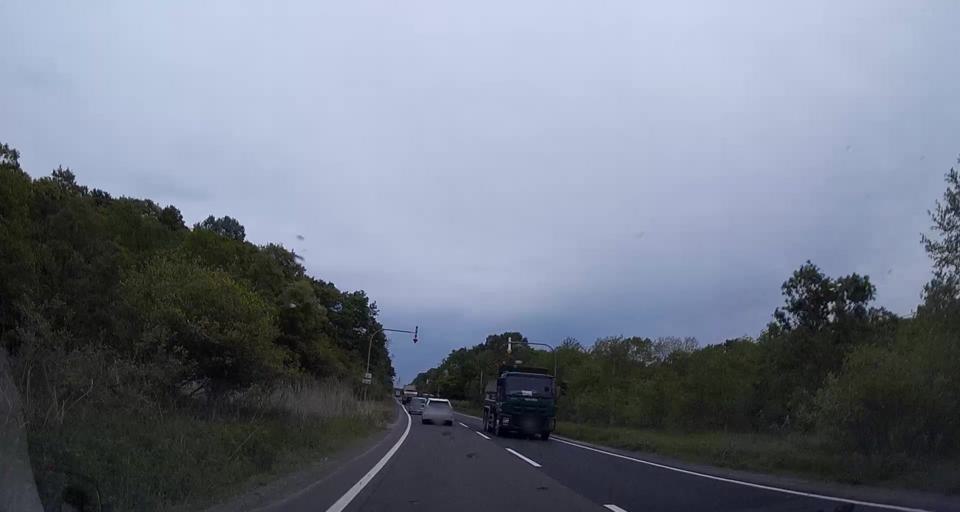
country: JP
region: Hokkaido
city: Chitose
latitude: 42.7075
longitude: 141.7446
